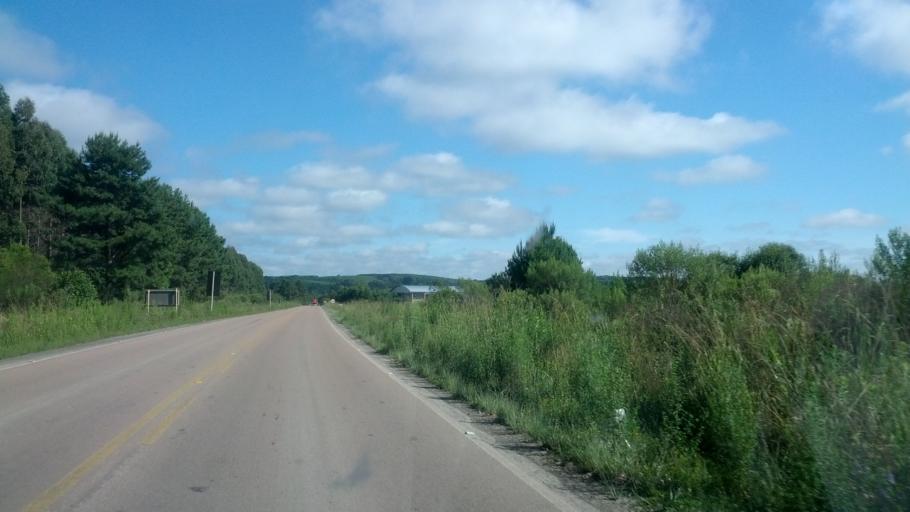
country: BR
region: Santa Catarina
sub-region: Otacilio Costa
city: Otacilio Costa
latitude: -27.4697
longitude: -50.1219
